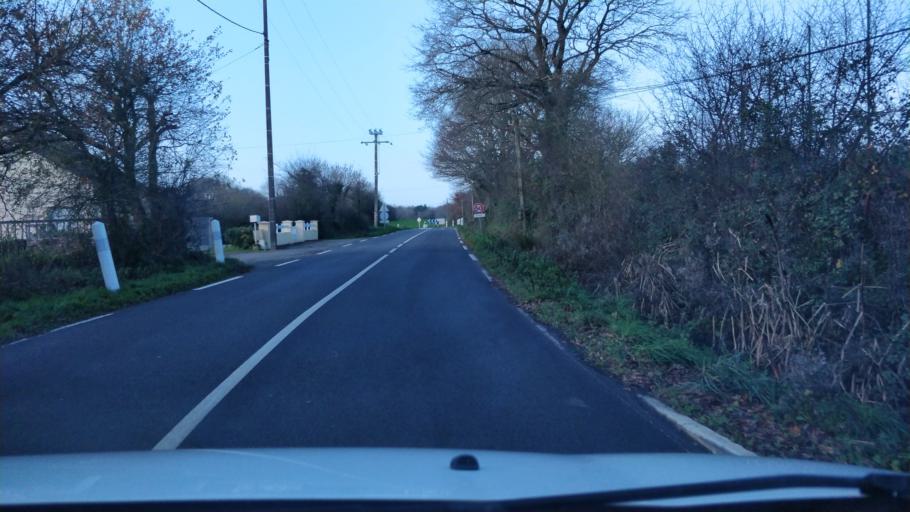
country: FR
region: Pays de la Loire
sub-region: Departement de la Loire-Atlantique
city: Asserac
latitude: 47.4201
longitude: -2.3968
